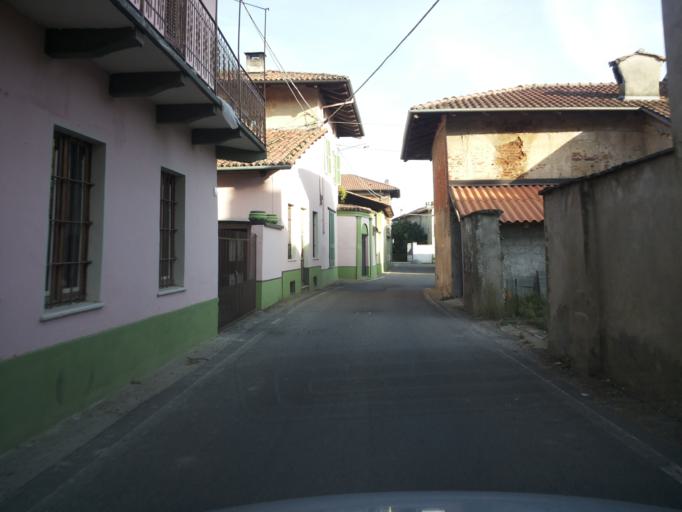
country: IT
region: Piedmont
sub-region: Provincia di Biella
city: Salussola
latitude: 45.4454
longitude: 8.1530
